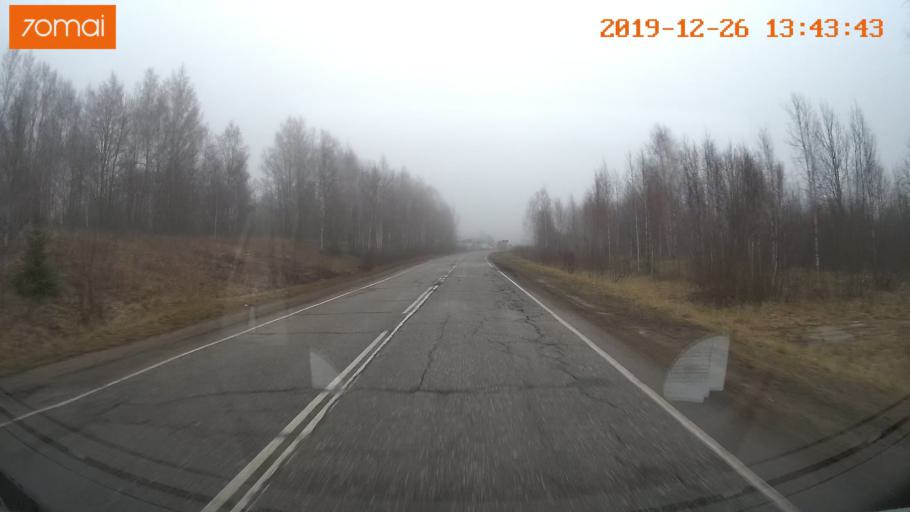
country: RU
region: Vologda
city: Sheksna
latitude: 58.7074
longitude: 38.4961
